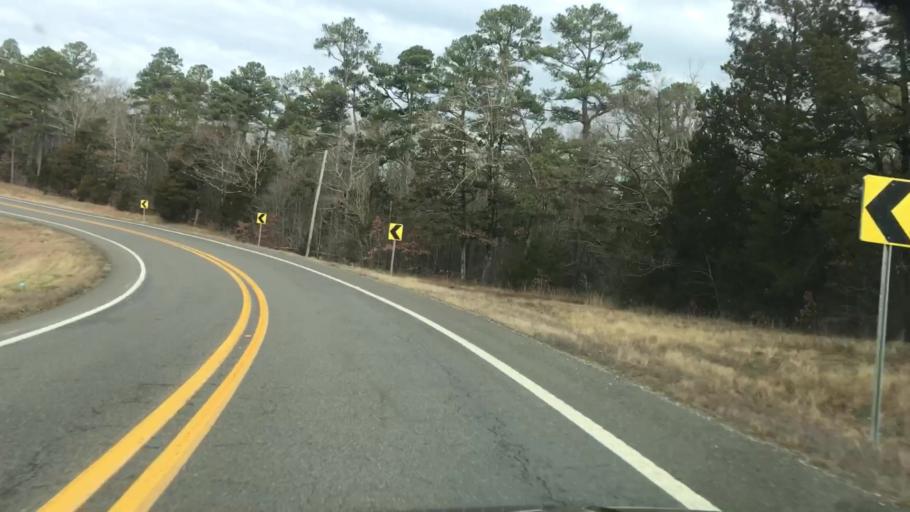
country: US
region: Arkansas
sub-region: Montgomery County
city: Mount Ida
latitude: 34.6194
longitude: -93.7042
